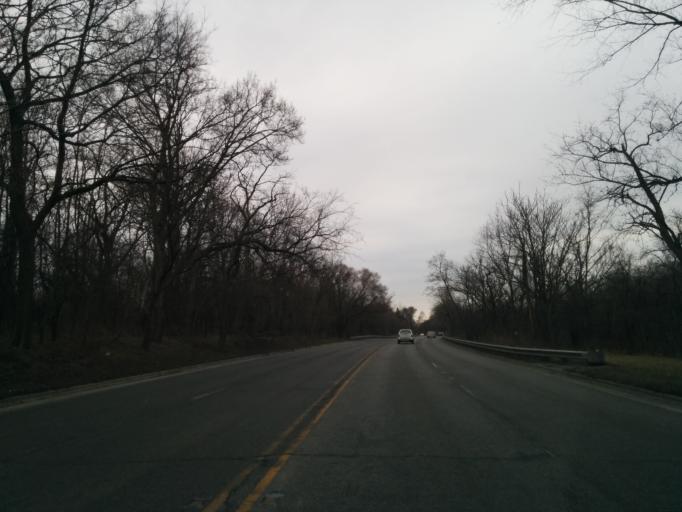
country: US
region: Illinois
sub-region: Cook County
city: Westchester
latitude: 41.8451
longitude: -87.8792
